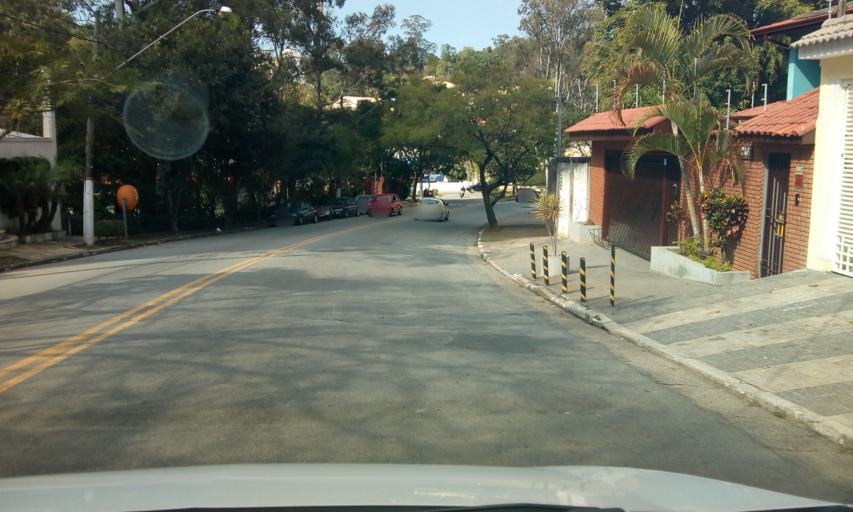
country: BR
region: Sao Paulo
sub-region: Osasco
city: Osasco
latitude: -23.5588
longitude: -46.7678
